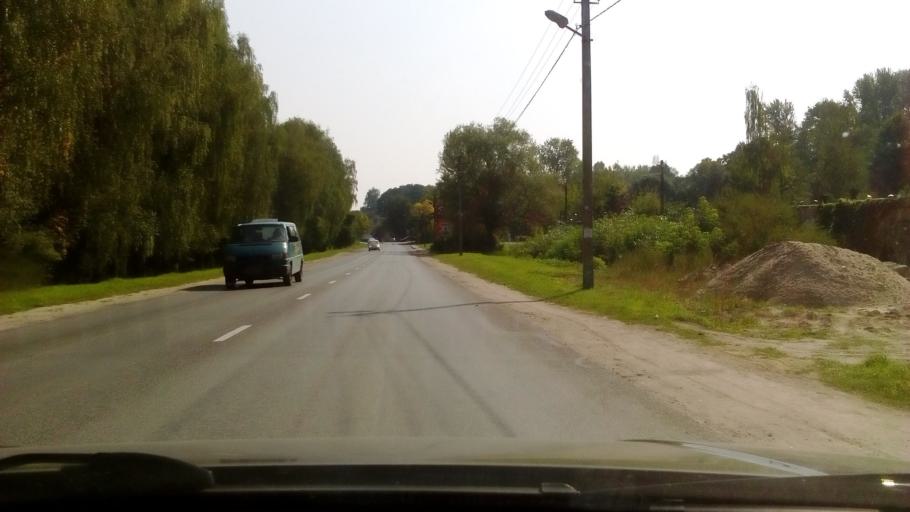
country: LT
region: Alytaus apskritis
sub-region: Alytus
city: Alytus
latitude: 54.4047
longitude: 24.0356
